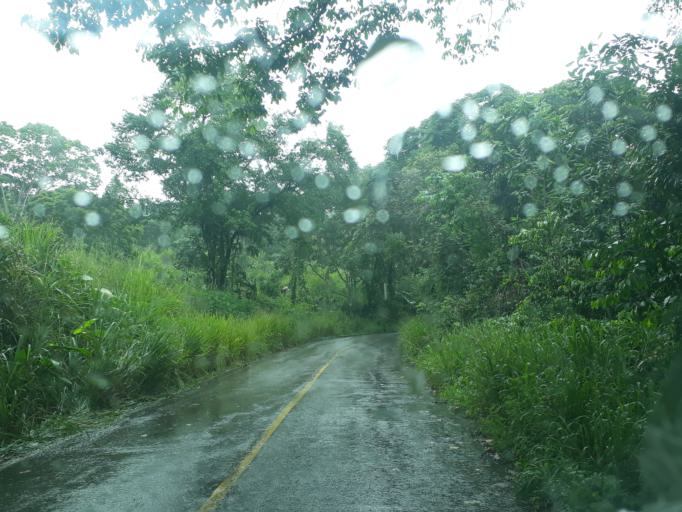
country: CO
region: Cundinamarca
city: Paratebueno
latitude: 4.4013
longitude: -73.3049
